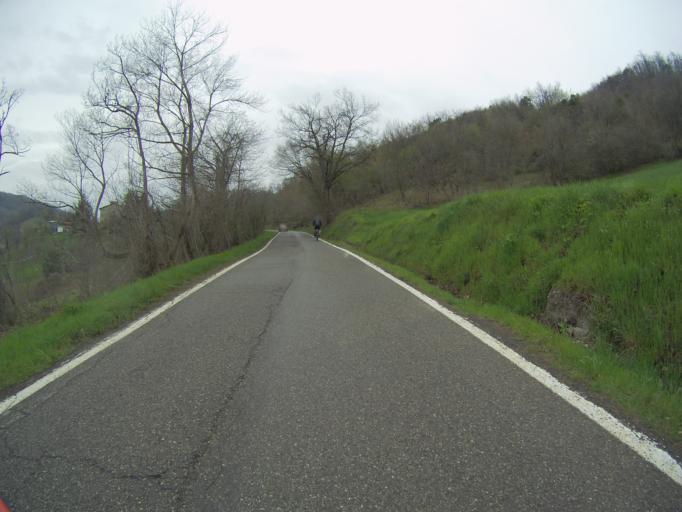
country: IT
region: Emilia-Romagna
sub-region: Provincia di Reggio Emilia
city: Casina
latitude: 44.5437
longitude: 10.4649
